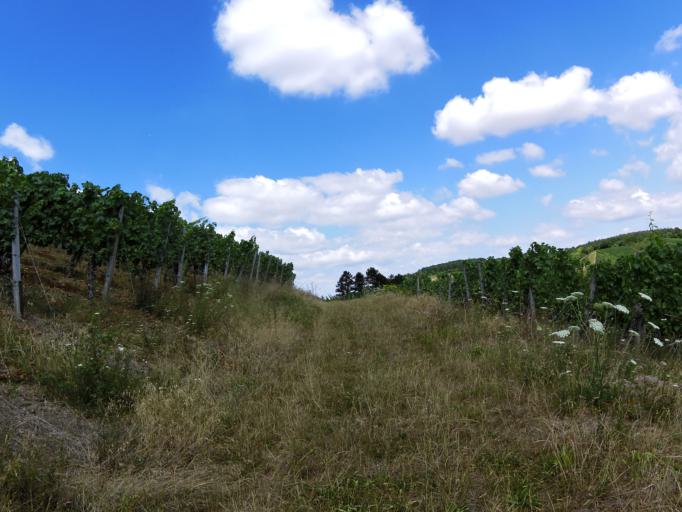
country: DE
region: Bavaria
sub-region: Regierungsbezirk Unterfranken
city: Gerbrunn
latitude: 49.7715
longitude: 9.9926
